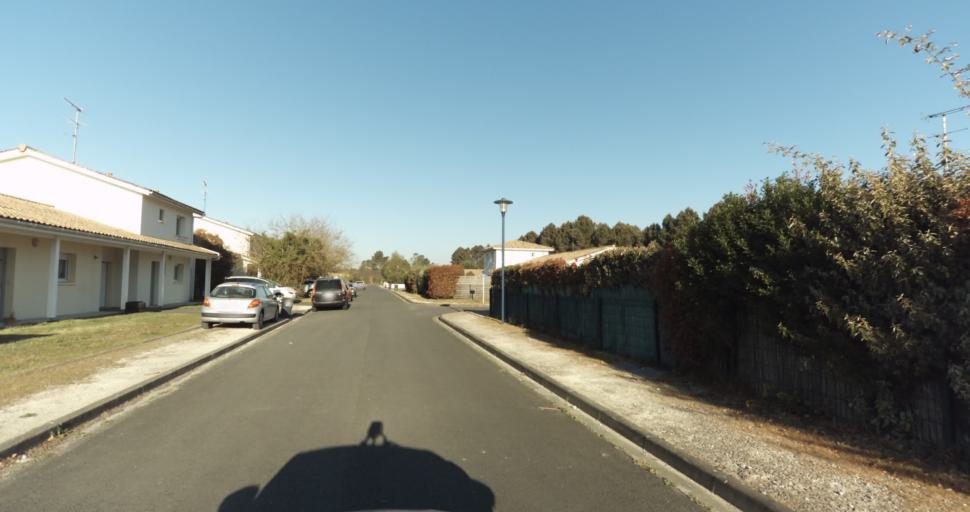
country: FR
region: Aquitaine
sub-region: Departement de la Gironde
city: Martignas-sur-Jalle
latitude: 44.8152
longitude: -0.7886
